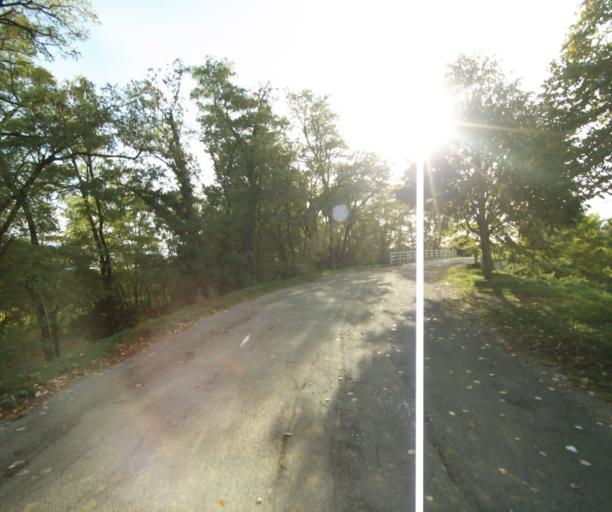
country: FR
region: Midi-Pyrenees
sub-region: Departement du Gers
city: Gondrin
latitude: 43.8977
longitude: 0.2511
